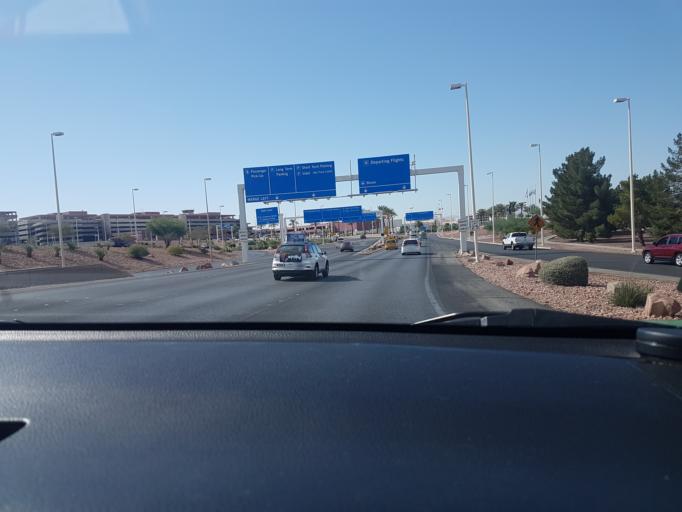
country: US
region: Nevada
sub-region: Clark County
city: Paradise
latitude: 36.0904
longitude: -115.1488
